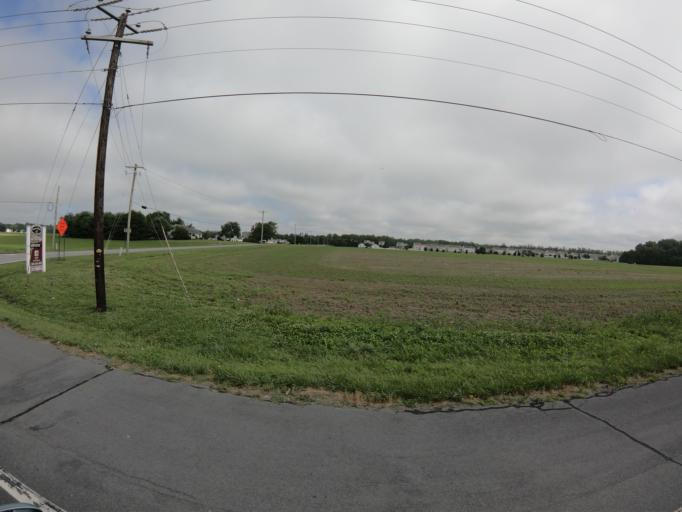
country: US
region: Delaware
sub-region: Kent County
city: Felton
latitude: 39.0067
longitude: -75.5543
